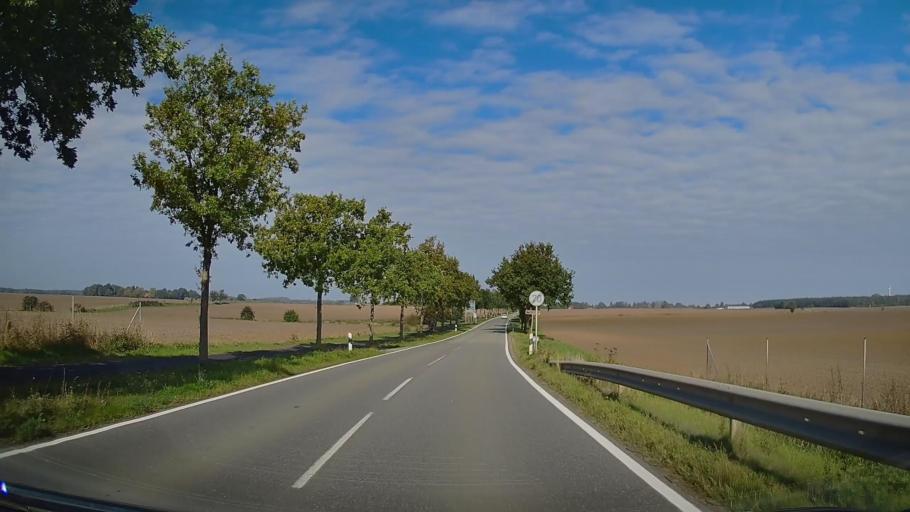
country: DE
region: Schleswig-Holstein
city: Oldenburg in Holstein
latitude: 54.3027
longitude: 10.8873
